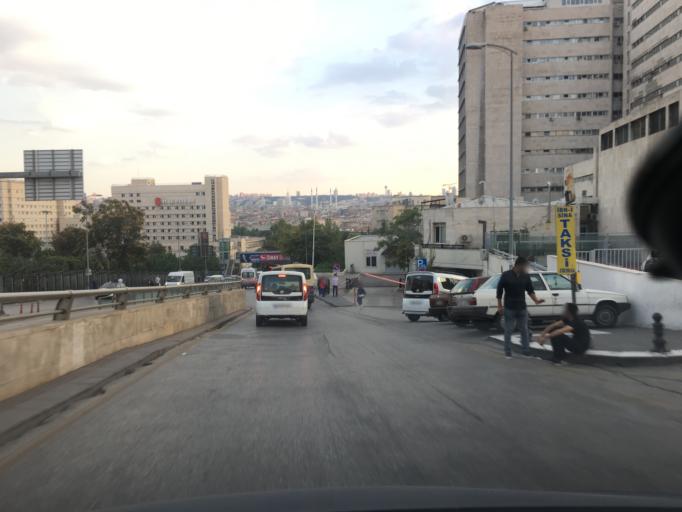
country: TR
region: Ankara
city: Ankara
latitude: 39.9329
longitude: 32.8597
